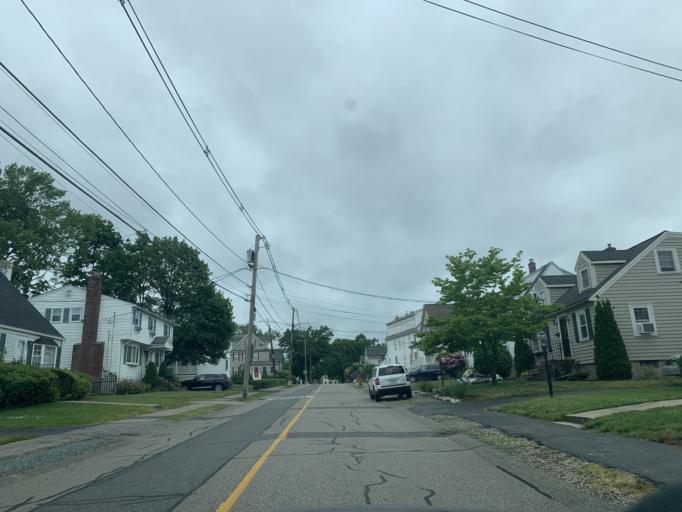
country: US
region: Massachusetts
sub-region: Norfolk County
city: Norwood
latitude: 42.1968
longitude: -71.1929
